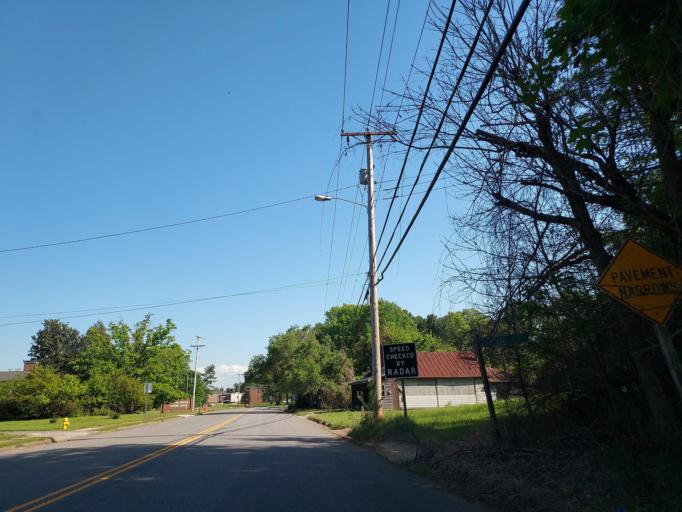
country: US
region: Virginia
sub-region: Amherst County
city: Madison Heights
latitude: 37.4163
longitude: -79.1210
